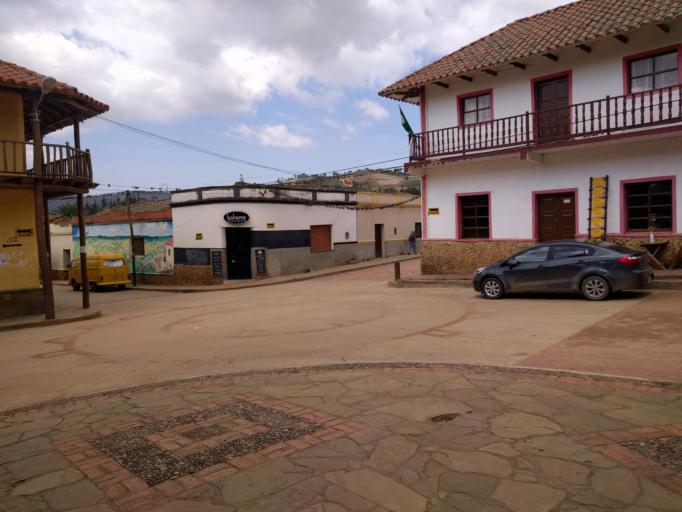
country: BO
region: Santa Cruz
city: Samaipata
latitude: -18.1800
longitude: -63.8760
